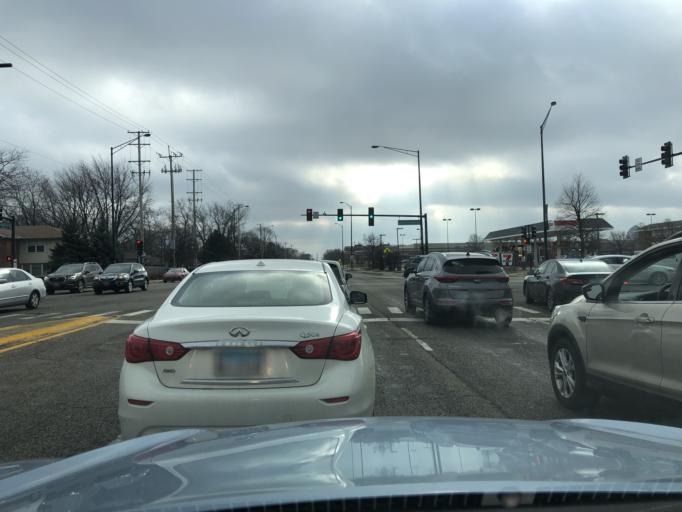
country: US
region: Illinois
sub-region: DuPage County
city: Itasca
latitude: 42.0040
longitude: -88.0038
